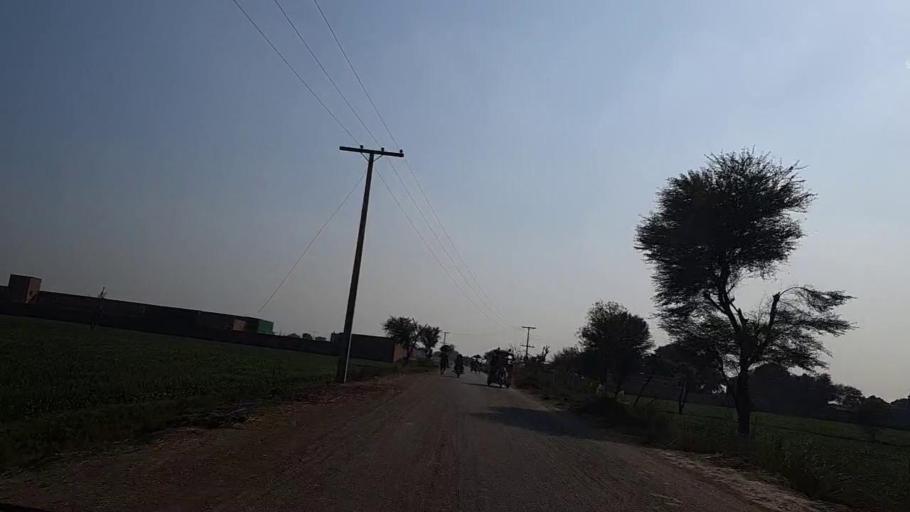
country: PK
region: Sindh
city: Sakrand
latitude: 26.1056
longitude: 68.2907
